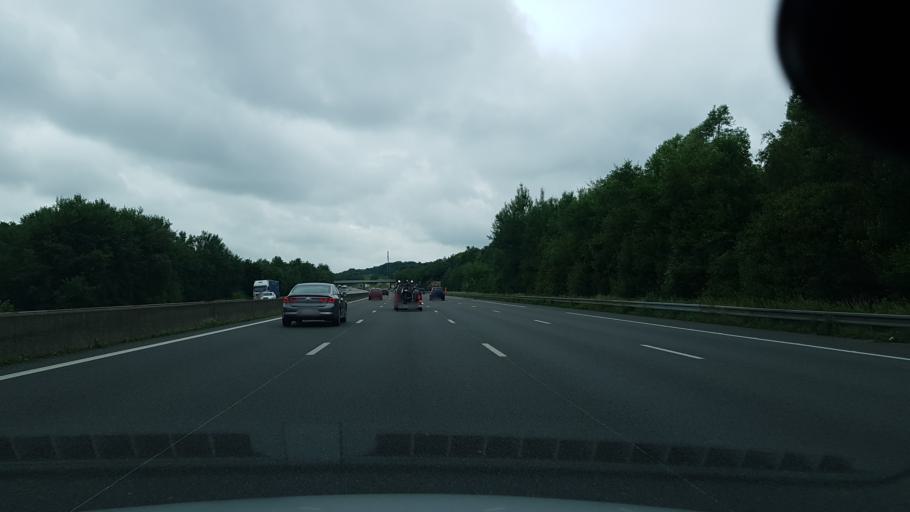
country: FR
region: Ile-de-France
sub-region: Departement de l'Essonne
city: Angervilliers
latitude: 48.6014
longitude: 2.0648
